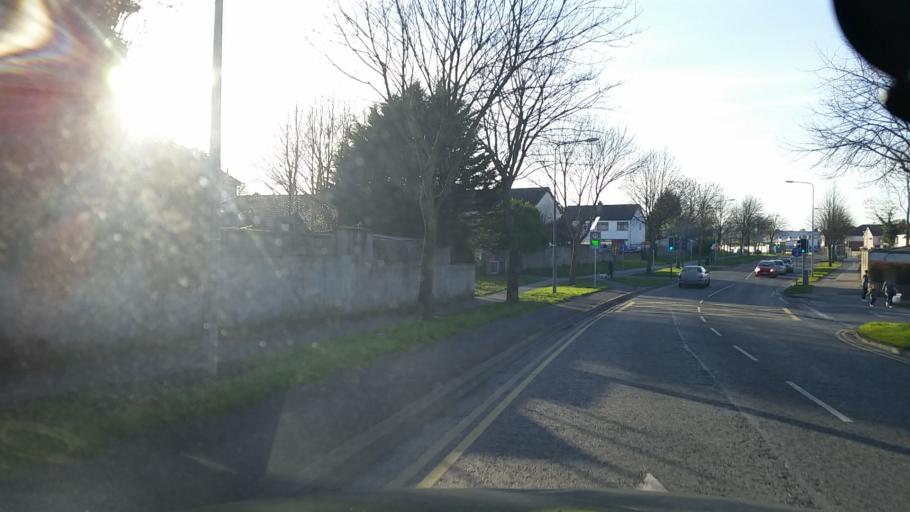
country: IE
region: Leinster
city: Hartstown
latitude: 53.4003
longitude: -6.4047
